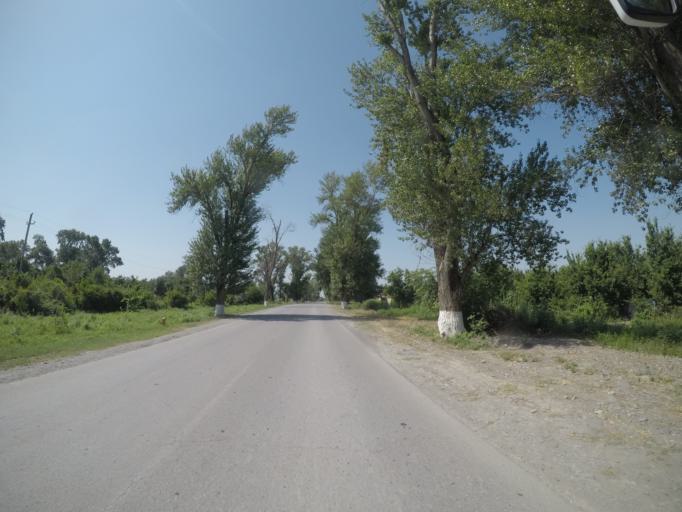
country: AZ
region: Agdas
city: Agdas
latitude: 40.6854
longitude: 47.5318
